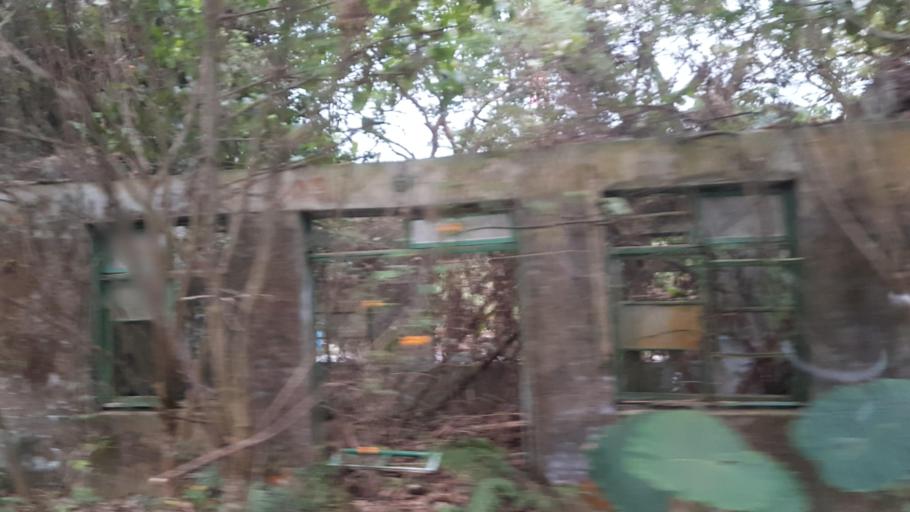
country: TW
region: Taiwan
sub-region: Chiayi
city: Jiayi Shi
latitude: 23.3278
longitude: 120.4868
